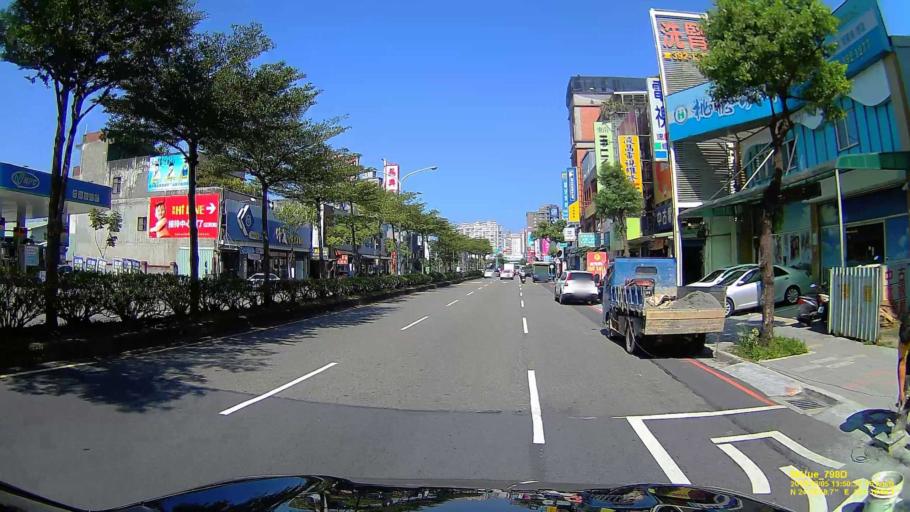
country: TW
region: Taiwan
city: Taoyuan City
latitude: 24.9831
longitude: 121.2779
